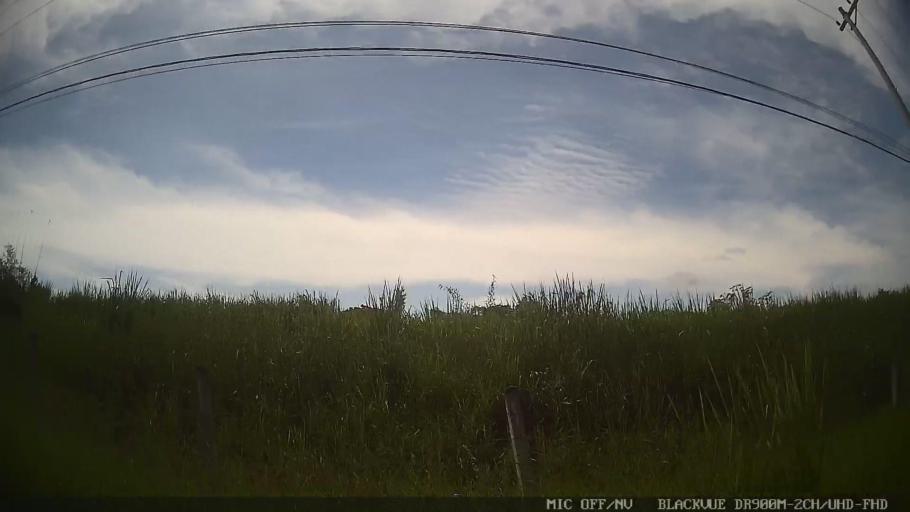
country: BR
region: Sao Paulo
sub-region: Santa Isabel
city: Santa Isabel
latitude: -23.3959
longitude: -46.1901
